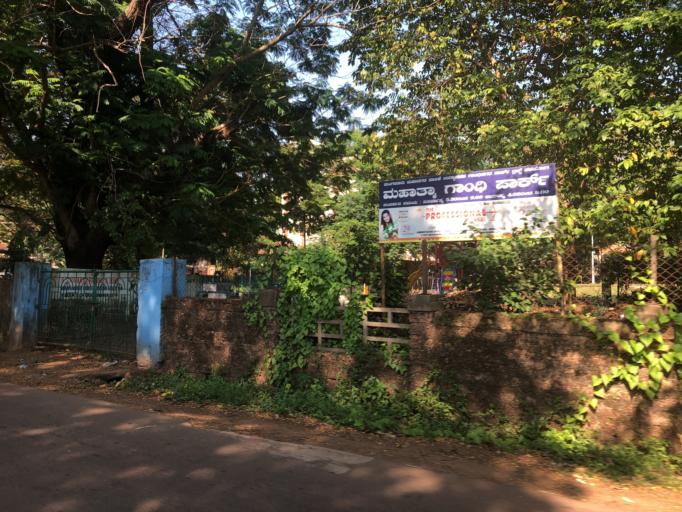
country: IN
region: Karnataka
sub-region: Dakshina Kannada
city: Mangalore
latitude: 12.8867
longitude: 74.8321
